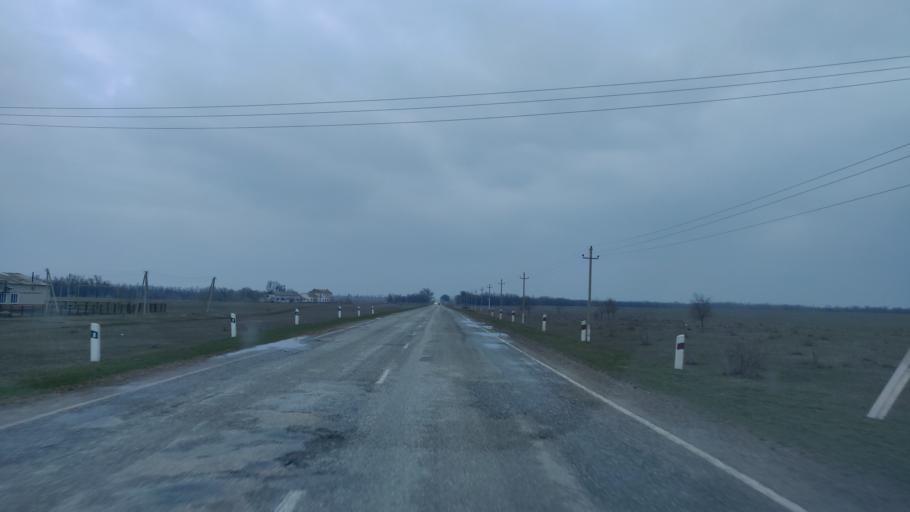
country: RU
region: Stavropol'skiy
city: Letnyaya Stavka
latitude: 45.3775
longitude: 43.3218
